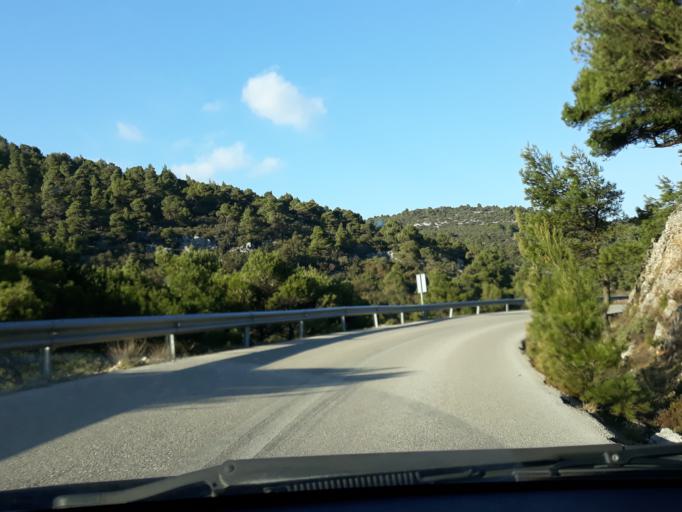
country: GR
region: Attica
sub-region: Nomarchia Dytikis Attikis
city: Fyli
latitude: 38.1539
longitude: 23.6293
